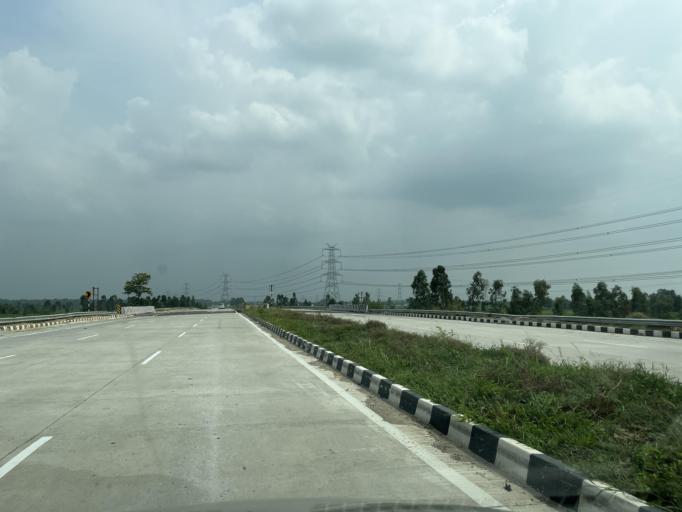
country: IN
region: Uttarakhand
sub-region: Udham Singh Nagar
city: Jaspur
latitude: 29.2888
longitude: 78.8534
